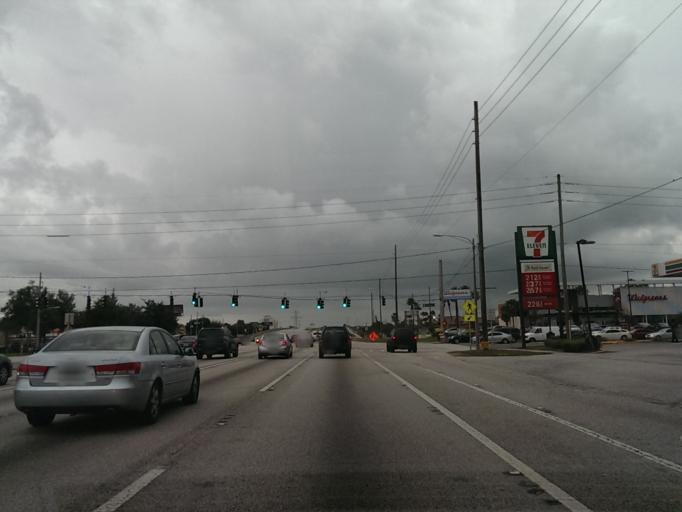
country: US
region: Florida
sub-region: Orange County
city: Tangelo Park
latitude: 28.4947
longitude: -81.4591
